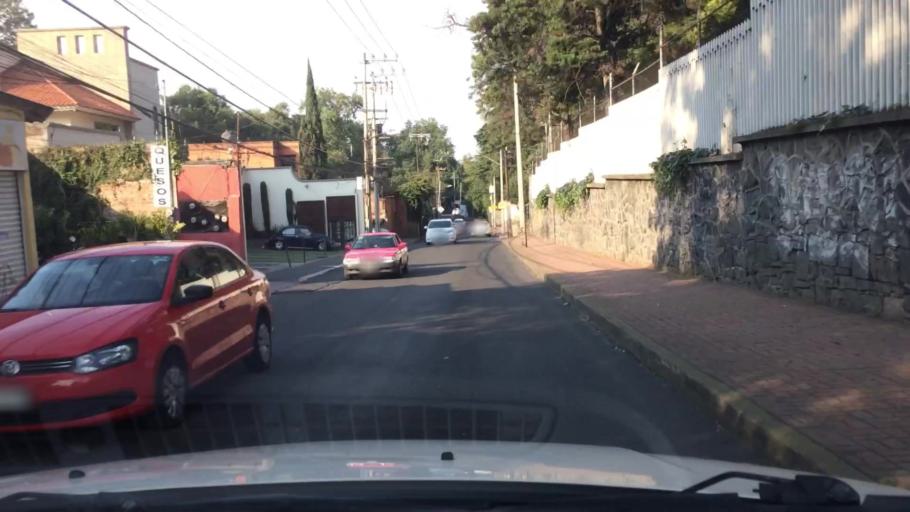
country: MX
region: Mexico City
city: Magdalena Contreras
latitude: 19.3266
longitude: -99.2162
